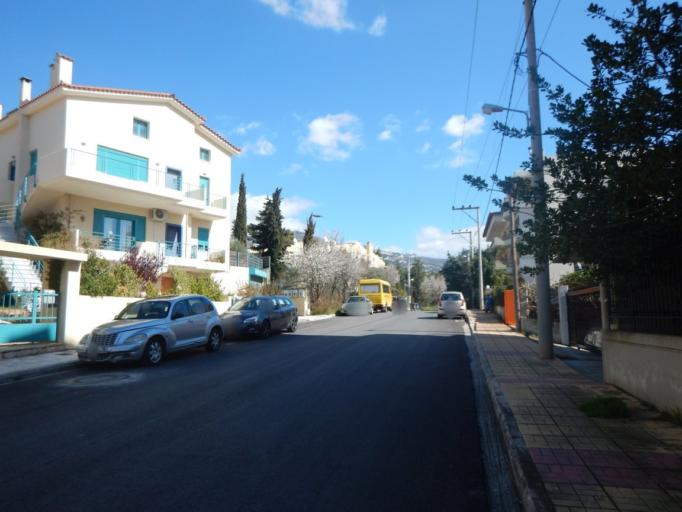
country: GR
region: Attica
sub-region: Nomarchia Athinas
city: Melissia
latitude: 38.0651
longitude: 23.8362
